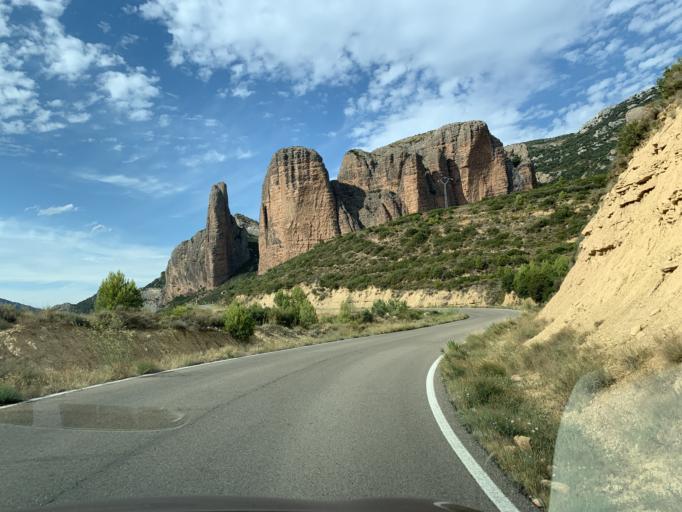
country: ES
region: Aragon
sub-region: Provincia de Zaragoza
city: Santa Eulalia de Gallego
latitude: 42.3417
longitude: -0.7297
